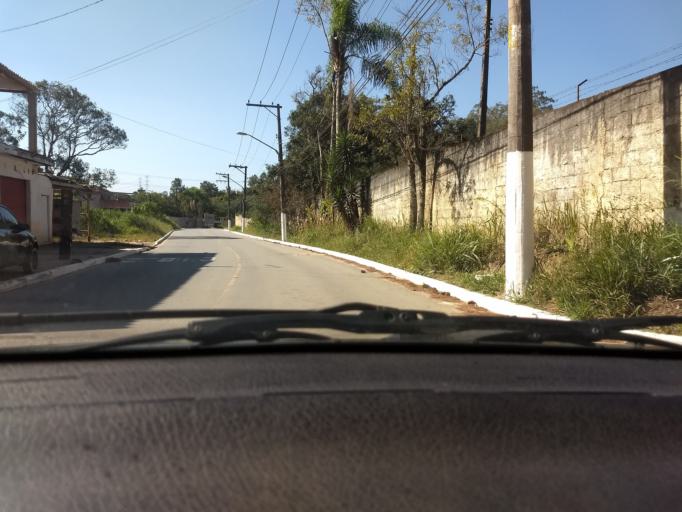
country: BR
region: Sao Paulo
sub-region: Embu-Guacu
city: Embu Guacu
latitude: -23.8086
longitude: -46.7449
